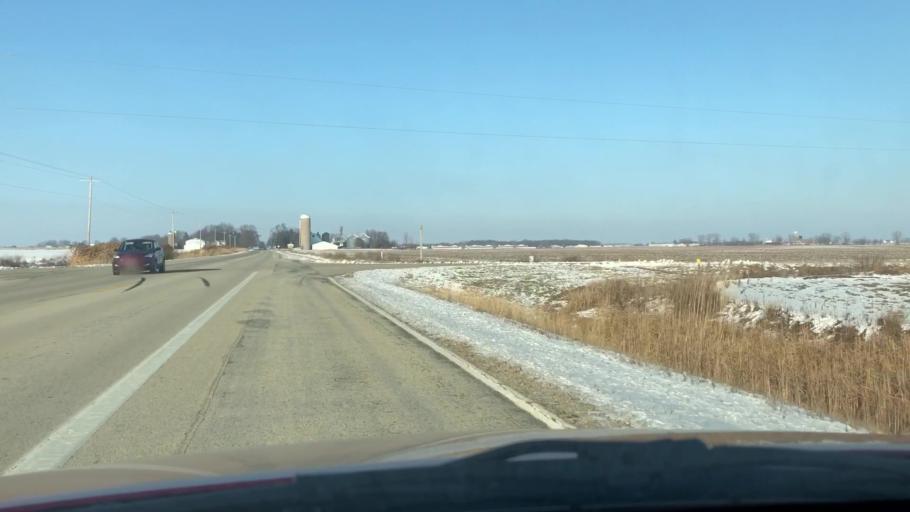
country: US
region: Wisconsin
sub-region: Outagamie County
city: Seymour
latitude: 44.4865
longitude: -88.3292
